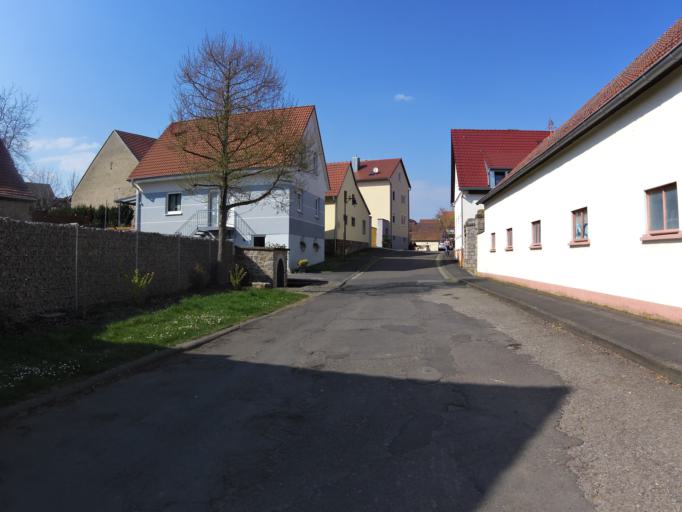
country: DE
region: Bavaria
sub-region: Regierungsbezirk Unterfranken
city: Prosselsheim
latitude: 49.8218
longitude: 10.1082
